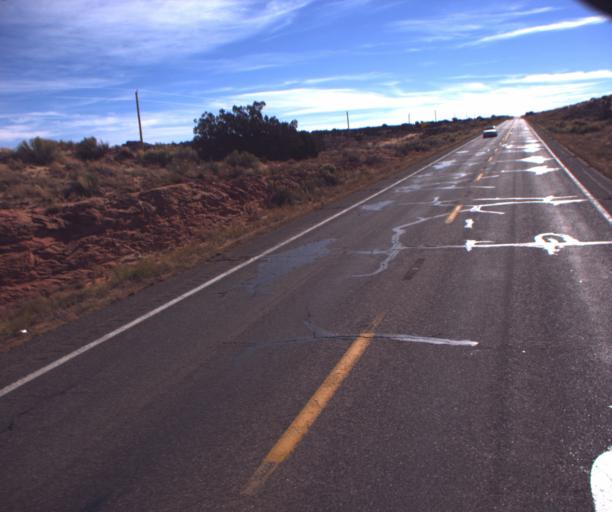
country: US
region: Arizona
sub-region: Coconino County
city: Kaibito
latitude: 36.6038
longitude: -111.1754
